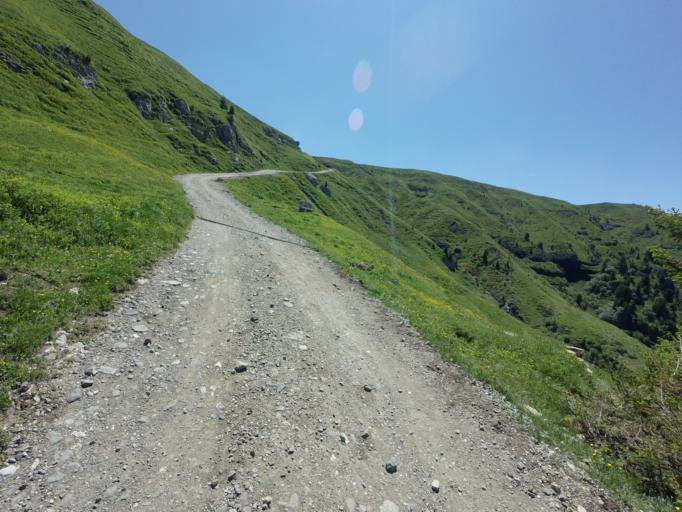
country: IT
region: Trentino-Alto Adige
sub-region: Provincia di Trento
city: Mazzin
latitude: 46.5081
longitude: 11.6964
